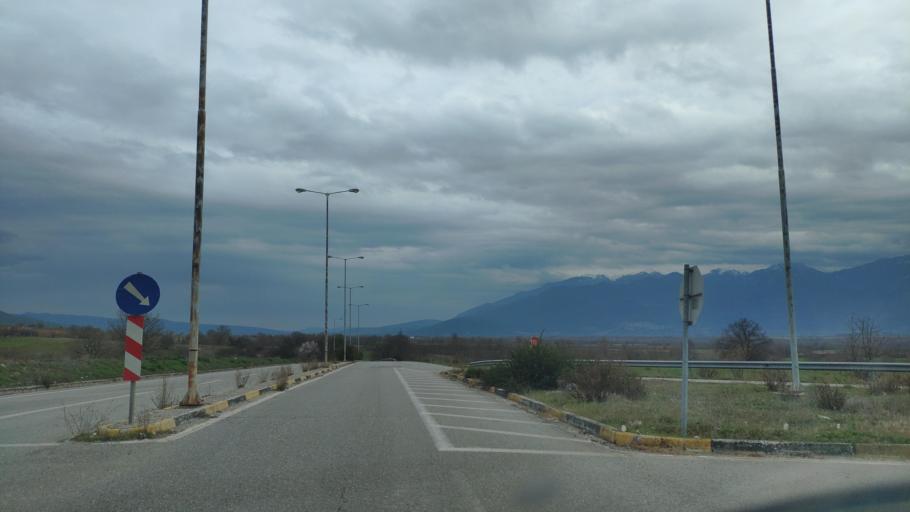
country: GR
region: Central Greece
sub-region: Nomos Fthiotidos
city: Anthili
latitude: 38.7125
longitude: 22.4615
